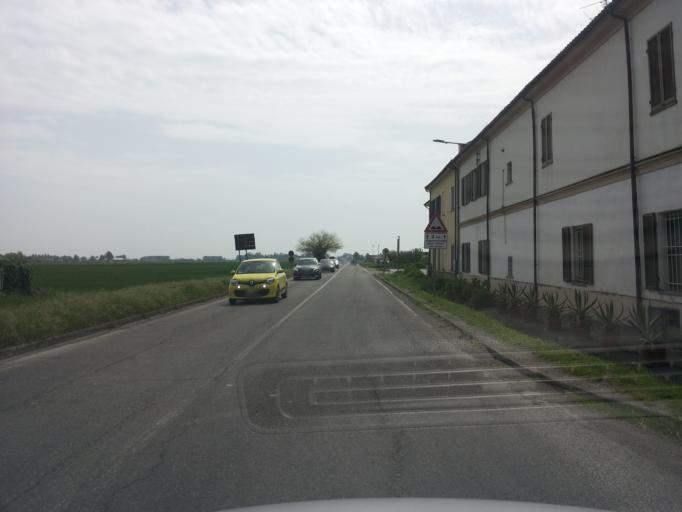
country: IT
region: Piedmont
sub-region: Provincia di Alessandria
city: Terruggia
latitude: 45.0862
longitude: 8.4695
